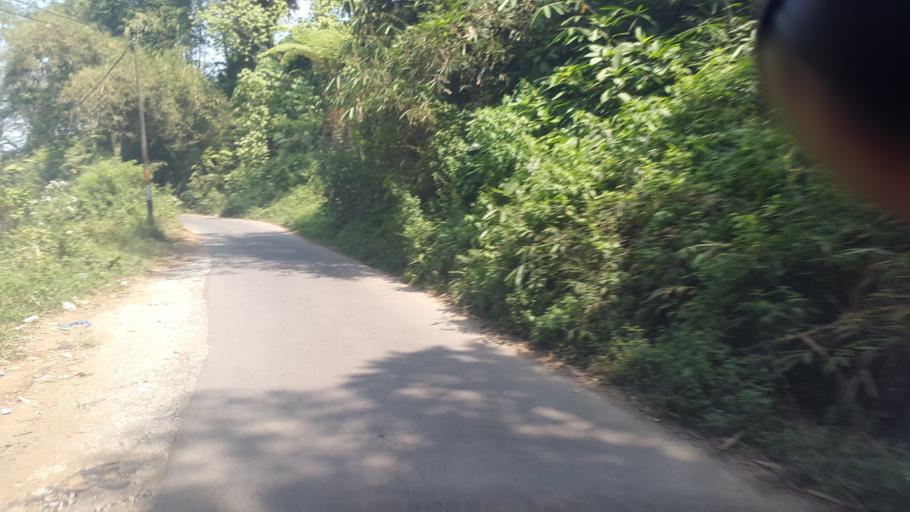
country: ID
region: West Java
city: Sukabumi
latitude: -6.8799
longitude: 106.9186
